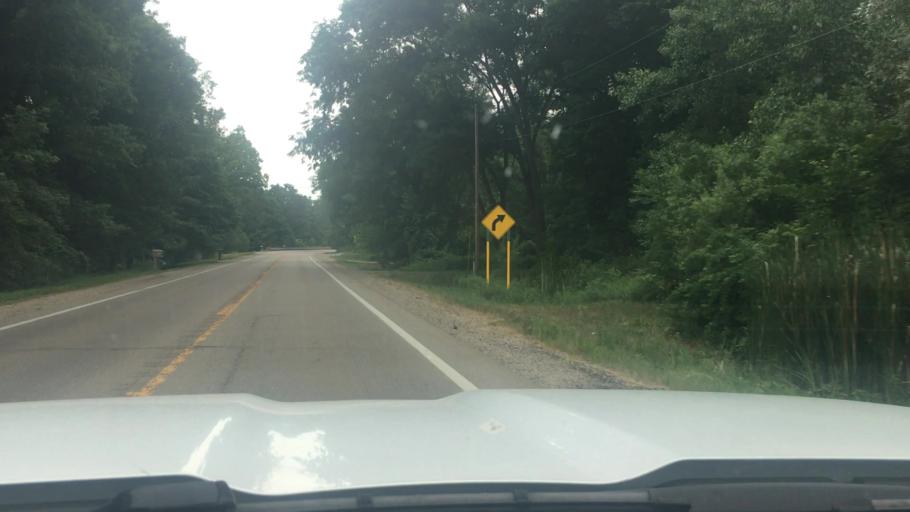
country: US
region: Michigan
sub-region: Ionia County
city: Saranac
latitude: 42.9320
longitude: -85.2421
